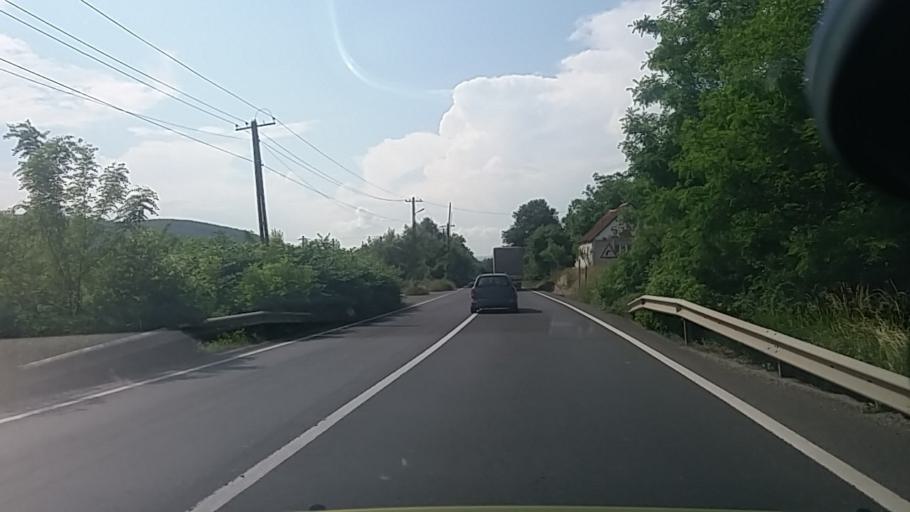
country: RO
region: Arad
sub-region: Comuna Bata
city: Bata
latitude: 46.0529
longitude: 22.0502
